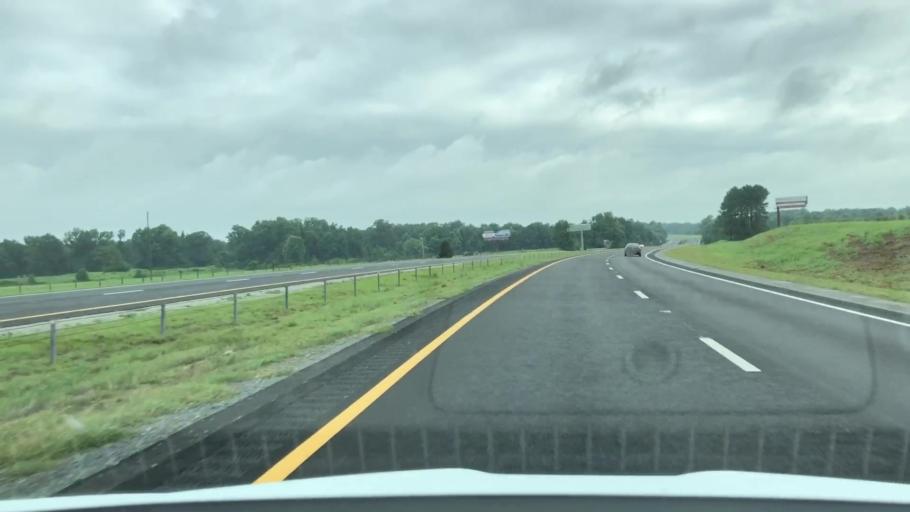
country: US
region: North Carolina
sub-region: Wayne County
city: Fremont
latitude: 35.5083
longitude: -77.9989
